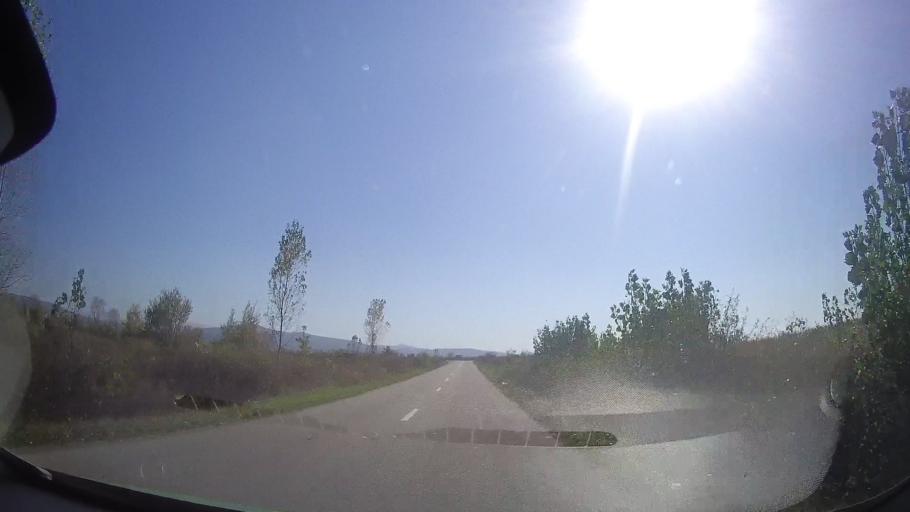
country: RO
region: Timis
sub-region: Comuna Traian Vuia
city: Traian Vuia
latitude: 45.7802
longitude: 22.0508
